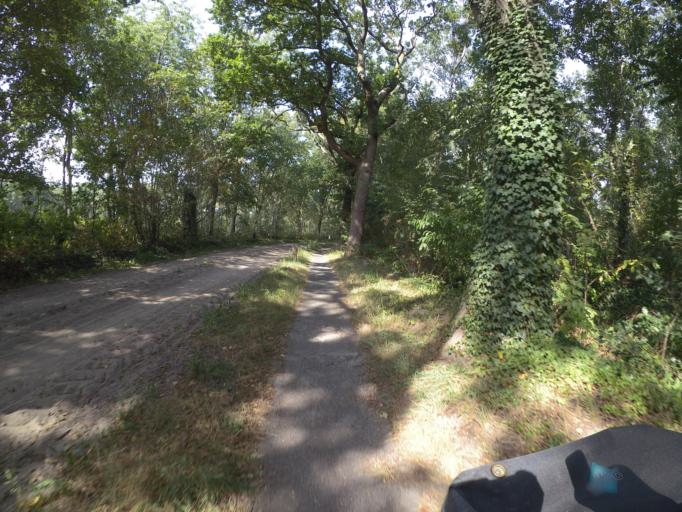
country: NL
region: Drenthe
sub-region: Gemeente Westerveld
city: Havelte
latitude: 52.7642
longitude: 6.2156
